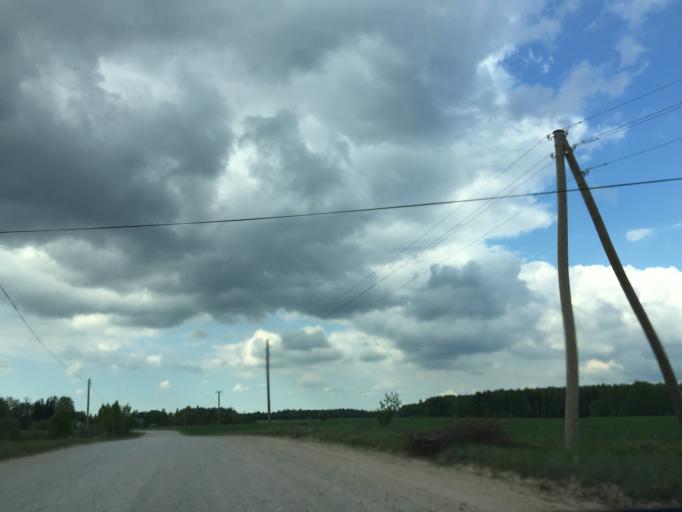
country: LV
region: Krimulda
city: Ragana
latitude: 57.3089
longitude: 24.7696
